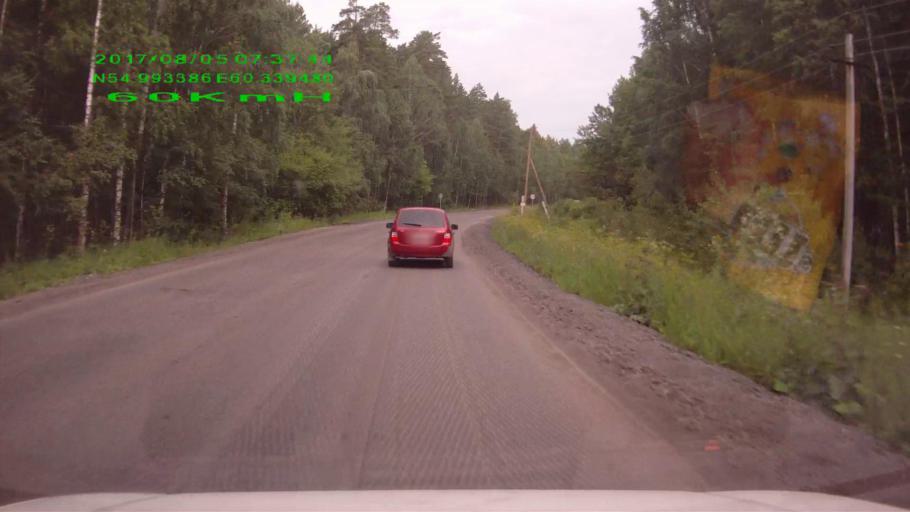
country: RU
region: Chelyabinsk
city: Chebarkul'
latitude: 54.9935
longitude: 60.3393
